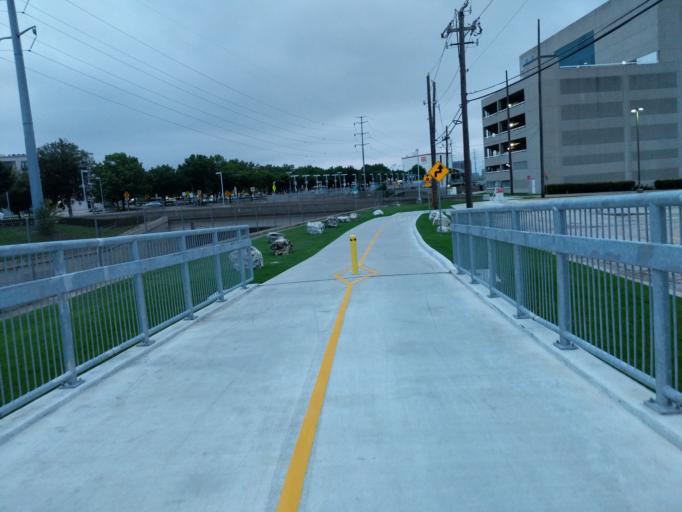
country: US
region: Texas
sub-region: Dallas County
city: Highland Park
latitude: 32.8392
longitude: -96.7736
